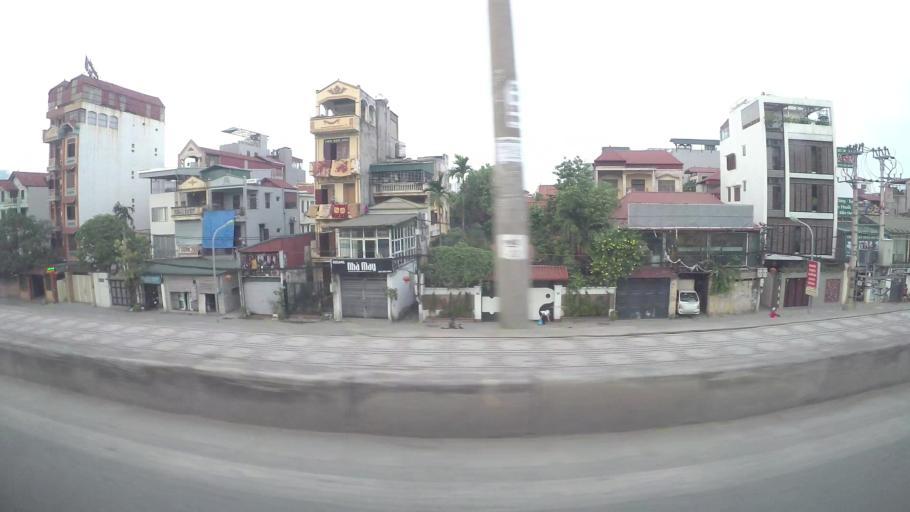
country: VN
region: Ha Noi
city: Hoan Kiem
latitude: 21.0359
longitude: 105.8720
